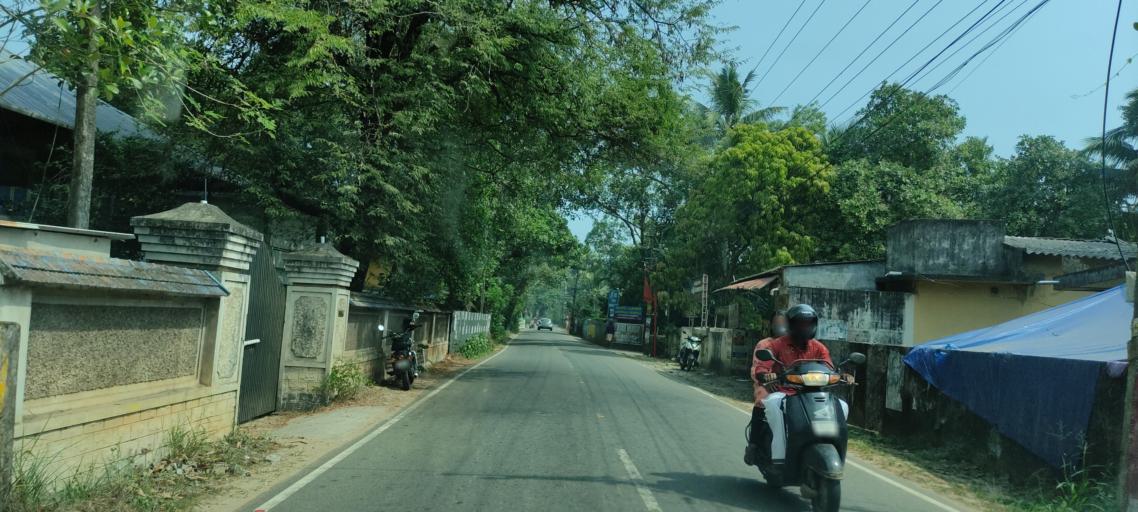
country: IN
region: Kerala
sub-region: Alappuzha
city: Shertallai
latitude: 9.6560
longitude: 76.3557
